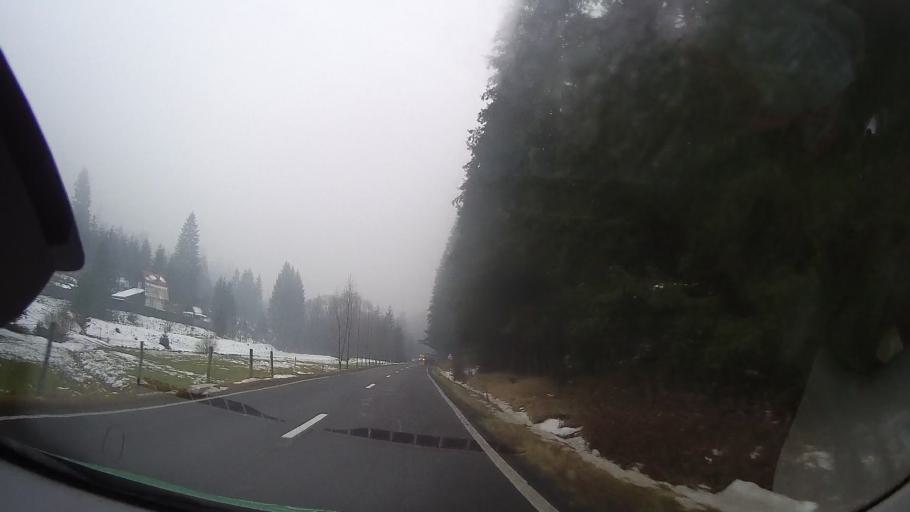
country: RO
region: Harghita
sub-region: Municipiul Gheorgheni
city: Gheorgheni
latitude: 46.7504
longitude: 25.6864
